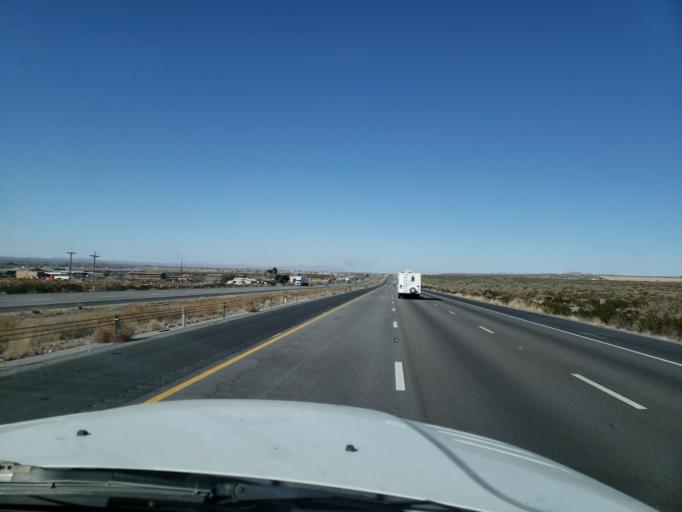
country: US
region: New Mexico
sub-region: Dona Ana County
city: Mesquite
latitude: 32.1603
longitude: -106.6599
